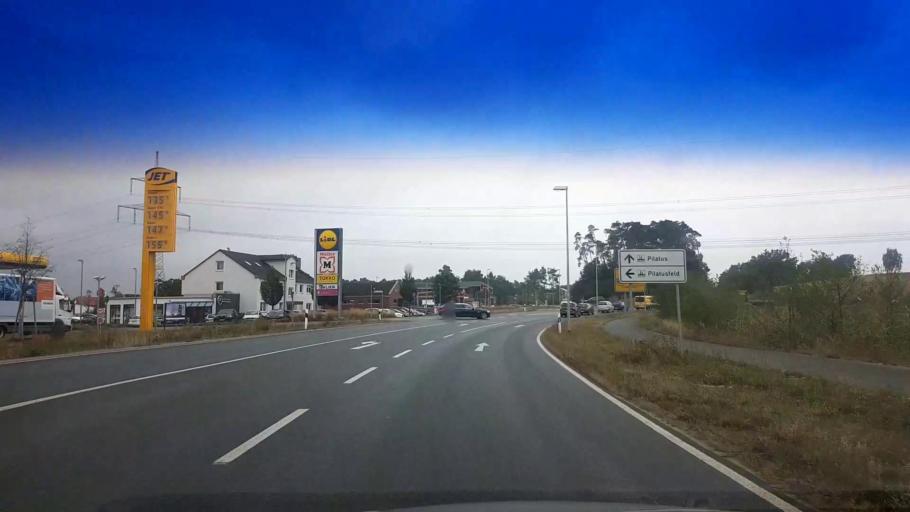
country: DE
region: Bavaria
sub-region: Upper Franconia
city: Hausen
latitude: 49.7025
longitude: 11.0423
